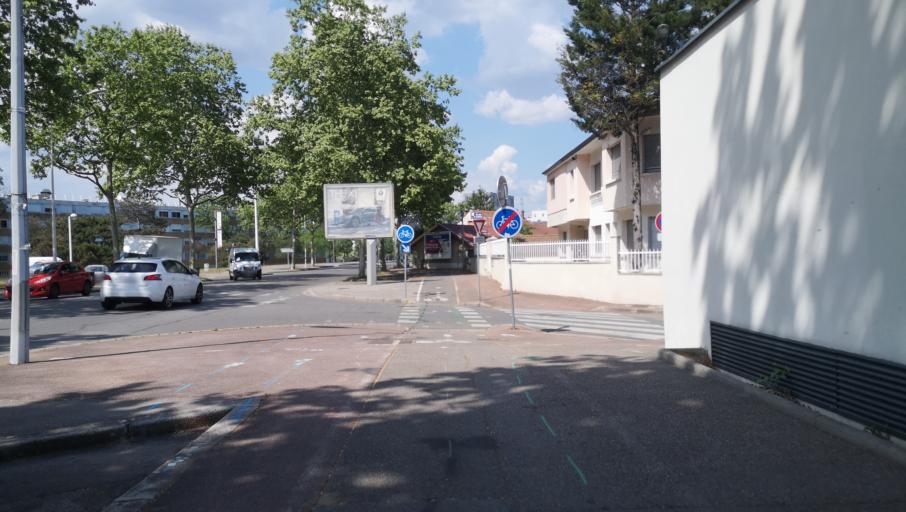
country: FR
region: Rhone-Alpes
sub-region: Departement du Rhone
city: Venissieux
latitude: 45.7282
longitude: 4.8870
